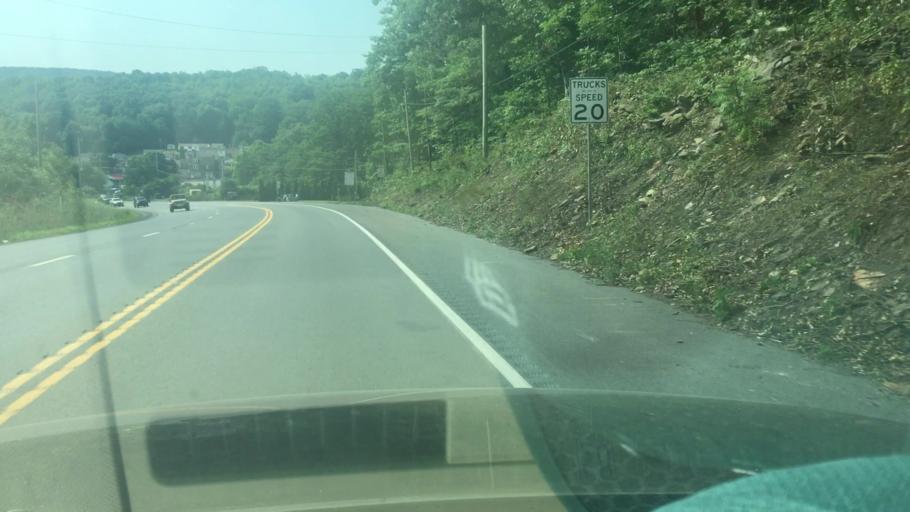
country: US
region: Pennsylvania
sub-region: Northumberland County
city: Mount Carmel
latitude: 40.8019
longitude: -76.4398
